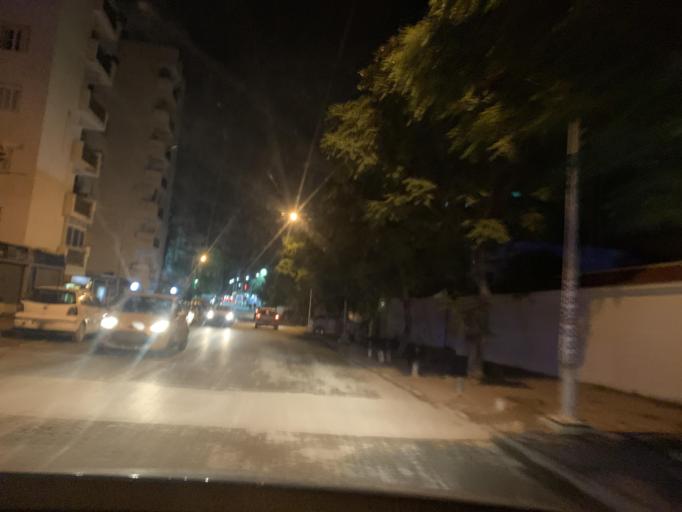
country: TN
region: Ariana
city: Ariana
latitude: 36.8579
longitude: 10.1836
